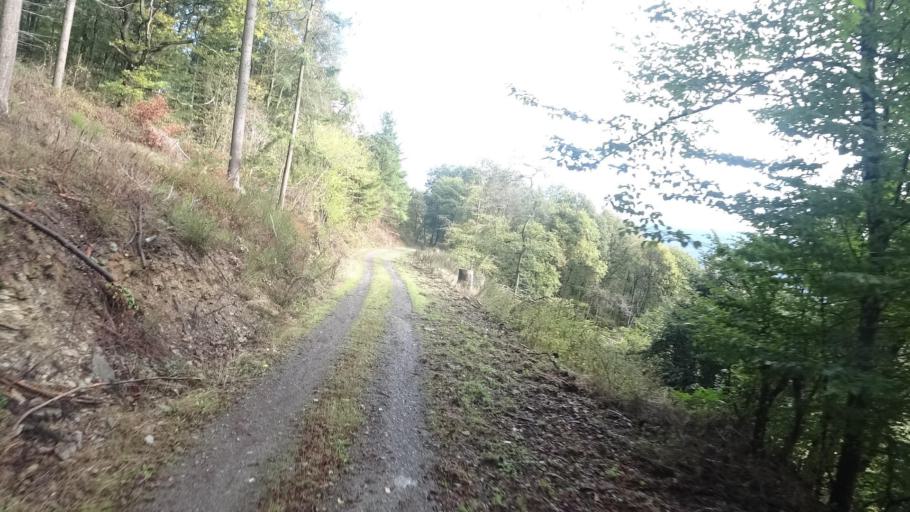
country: DE
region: Rheinland-Pfalz
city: Kamp-Bornhofen
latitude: 50.1933
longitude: 7.5972
